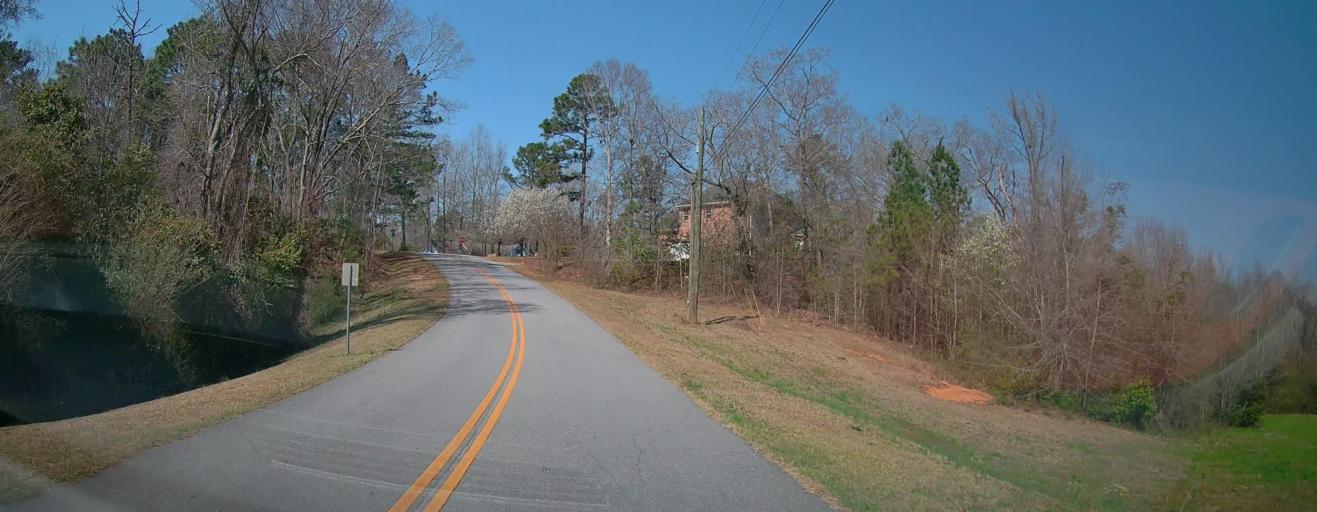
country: US
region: Georgia
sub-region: Houston County
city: Centerville
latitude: 32.5927
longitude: -83.6920
